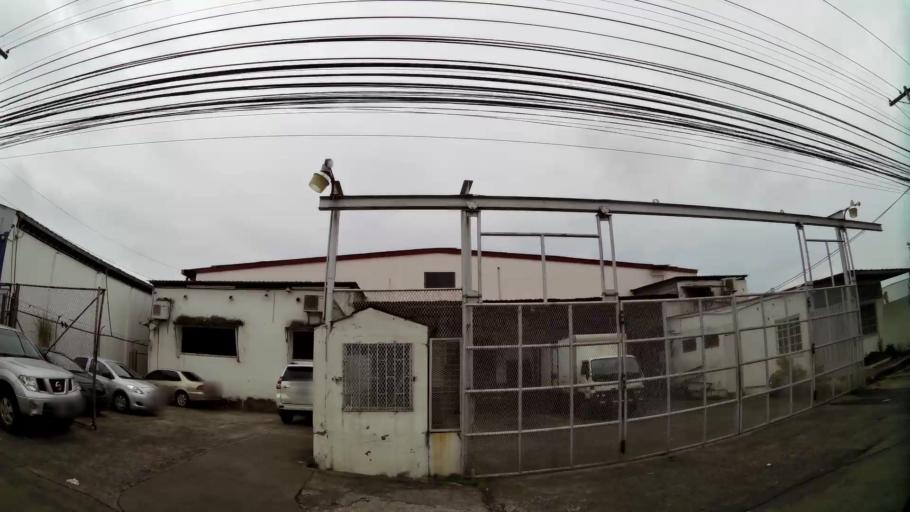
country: PA
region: Panama
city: Panama
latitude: 9.0005
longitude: -79.5272
